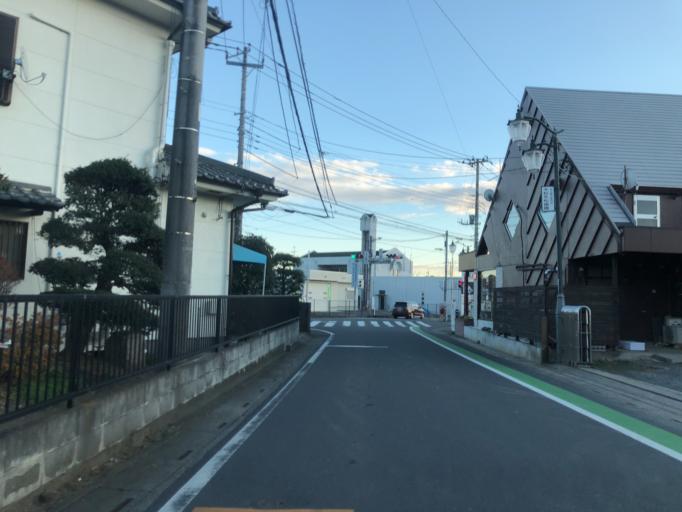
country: JP
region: Saitama
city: Fukiage-fujimi
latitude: 36.0509
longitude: 139.4056
